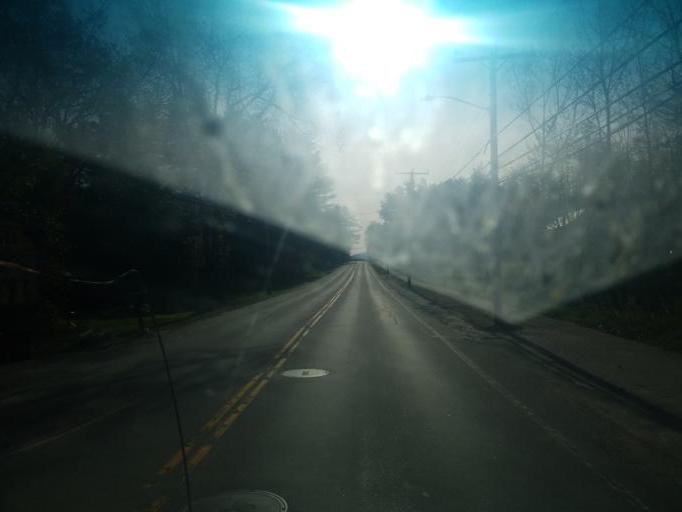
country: US
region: New Hampshire
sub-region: Grafton County
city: Deerfield
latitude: 44.2813
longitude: -71.6753
